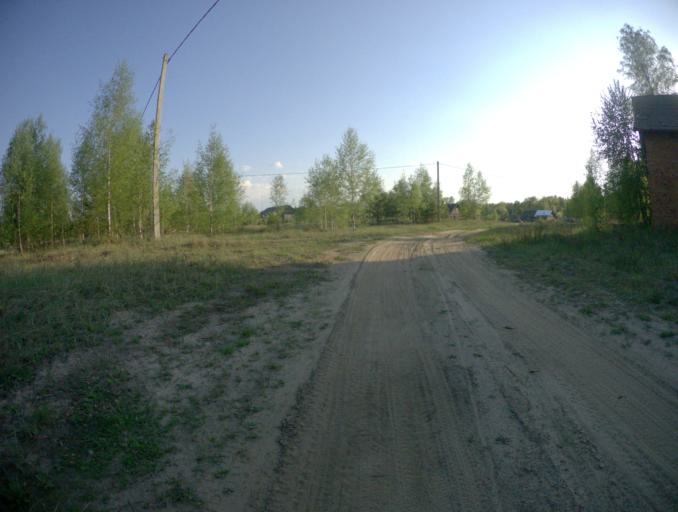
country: RU
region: Vladimir
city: Vyazniki
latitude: 56.3635
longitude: 42.1439
